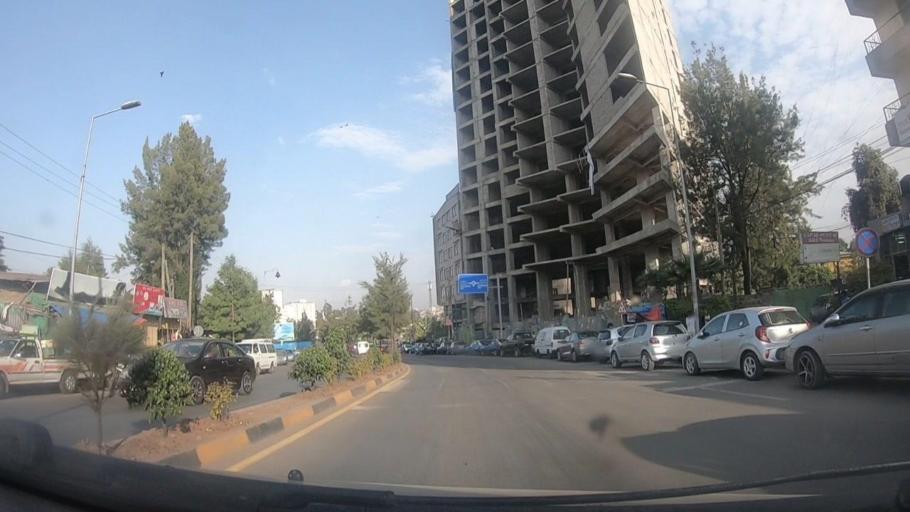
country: ET
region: Adis Abeba
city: Addis Ababa
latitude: 8.9824
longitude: 38.7332
